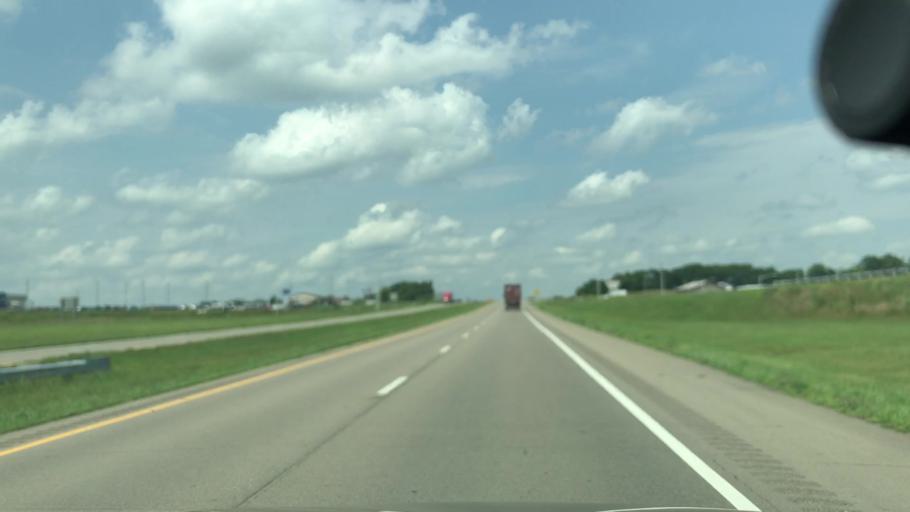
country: US
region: Ohio
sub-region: Ross County
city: Chillicothe
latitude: 39.4164
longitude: -82.9753
